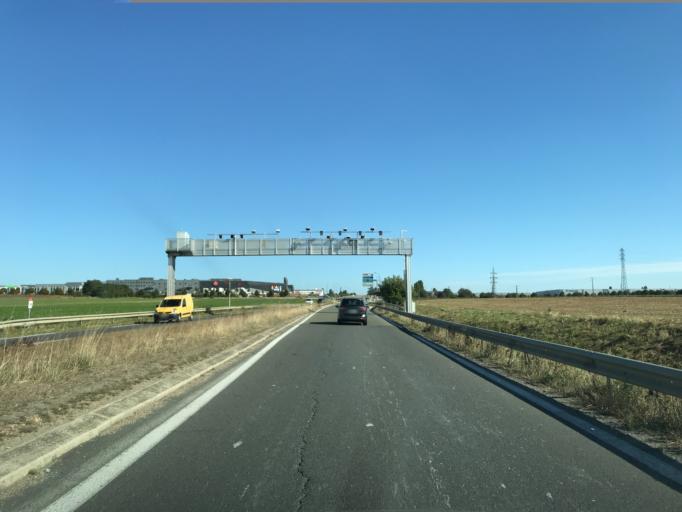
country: FR
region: Ile-de-France
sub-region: Departement de Seine-et-Marne
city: Chauconin-Neufmontiers
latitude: 48.9573
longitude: 2.8508
